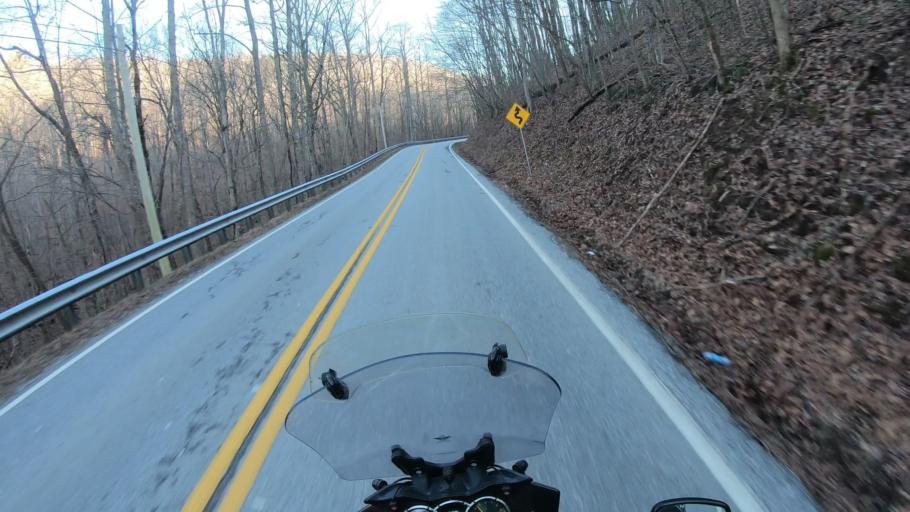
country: US
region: Georgia
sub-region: Union County
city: Blairsville
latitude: 34.7136
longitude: -84.0485
